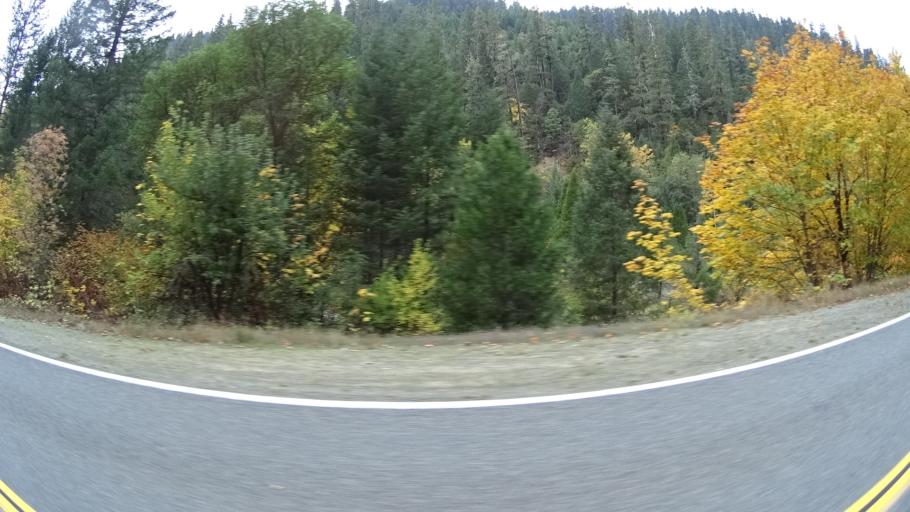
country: US
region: California
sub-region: Siskiyou County
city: Happy Camp
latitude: 41.8997
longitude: -123.4387
